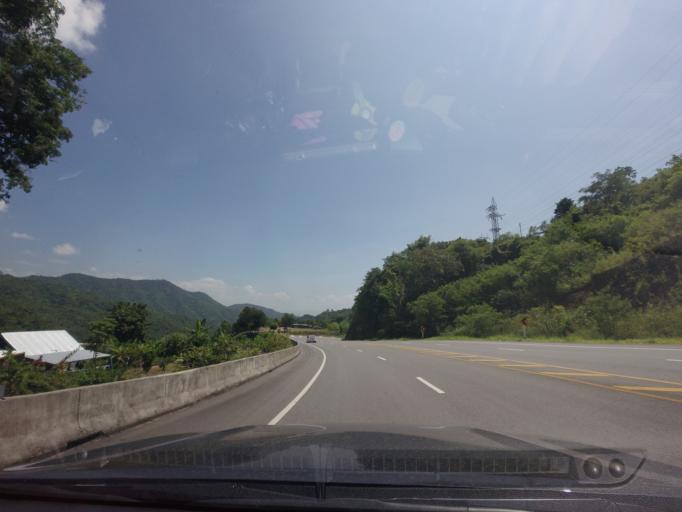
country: TH
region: Phetchabun
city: Khao Kho
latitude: 16.7827
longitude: 101.0968
